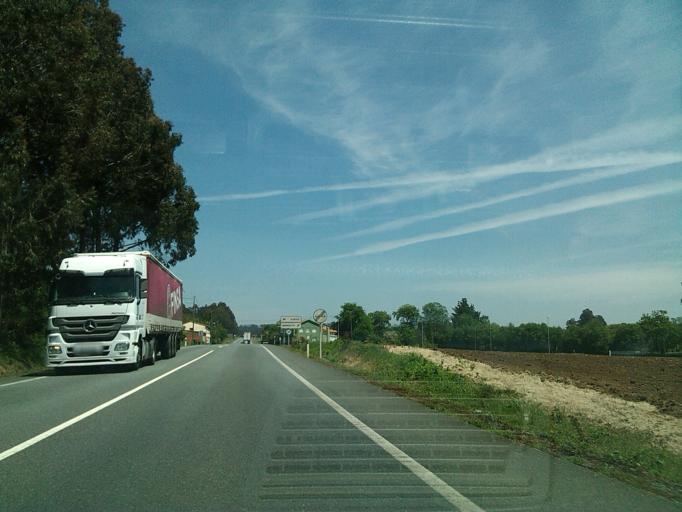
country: ES
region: Galicia
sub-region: Provincia da Coruna
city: Mesia
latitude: 43.0736
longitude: -8.1981
